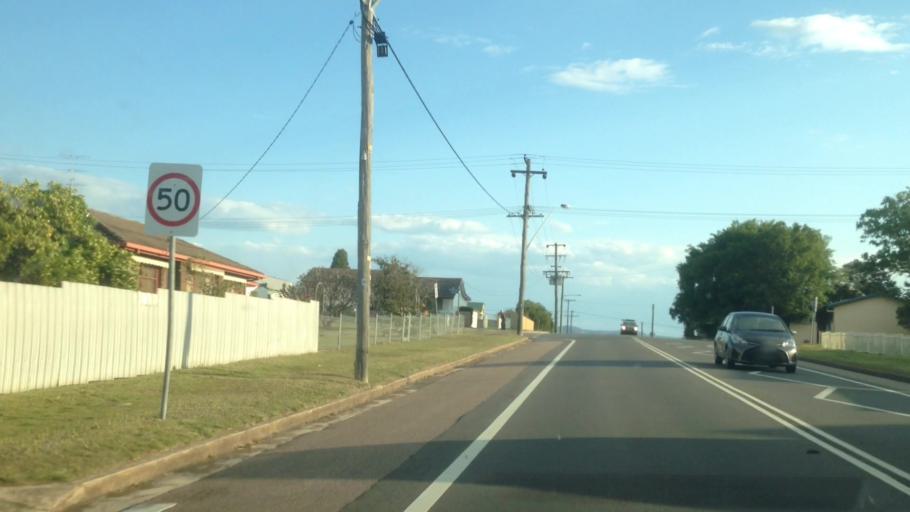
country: AU
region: New South Wales
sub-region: Cessnock
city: Kurri Kurri
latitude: -32.8303
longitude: 151.4811
